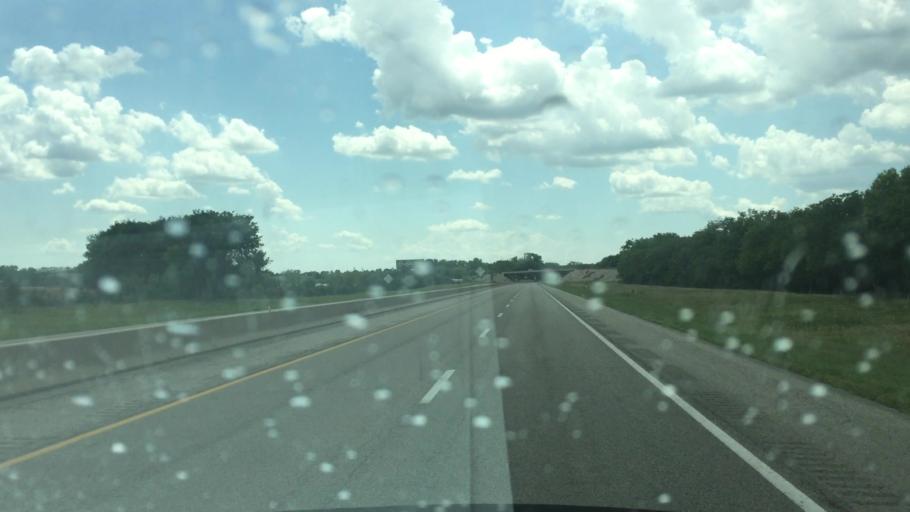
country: US
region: Kansas
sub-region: Shawnee County
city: Topeka
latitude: 38.9717
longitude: -95.7127
